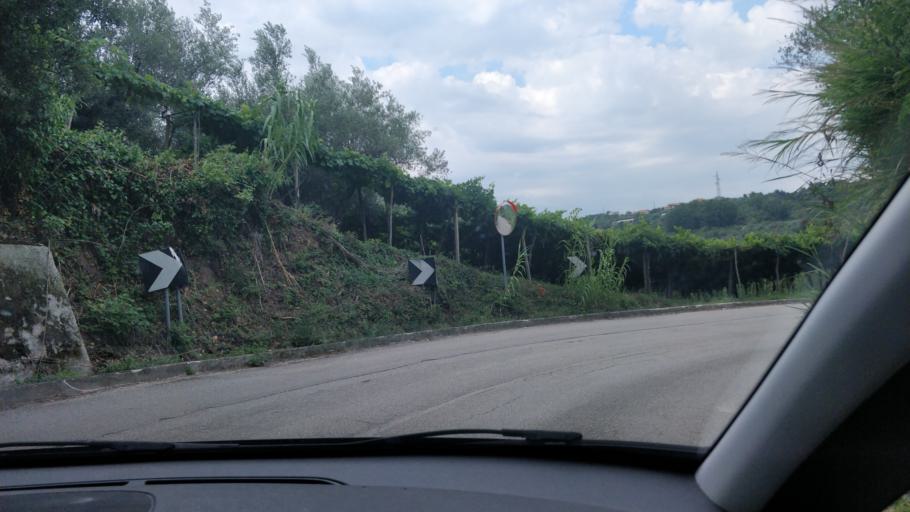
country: IT
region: Abruzzo
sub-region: Provincia di Chieti
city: Marina di San Vito
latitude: 42.3003
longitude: 14.4427
